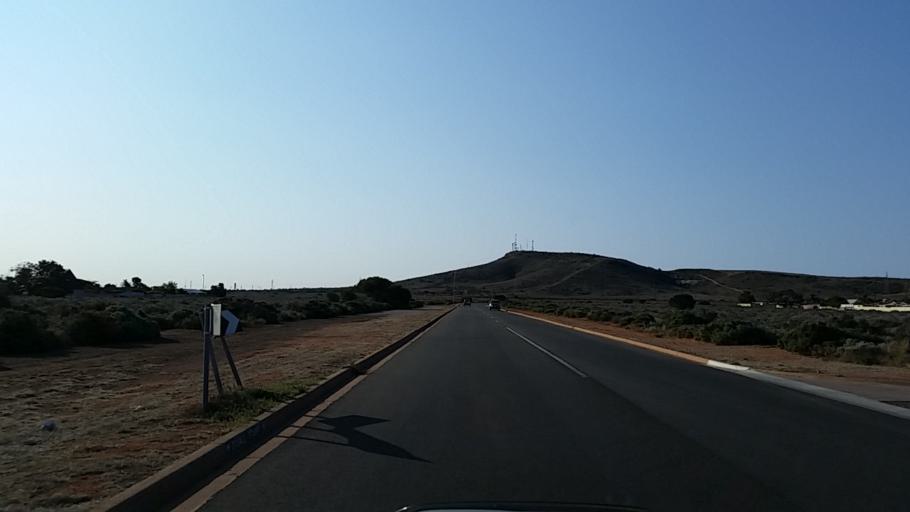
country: AU
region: South Australia
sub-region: Whyalla
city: Whyalla
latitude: -33.0135
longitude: 137.5289
